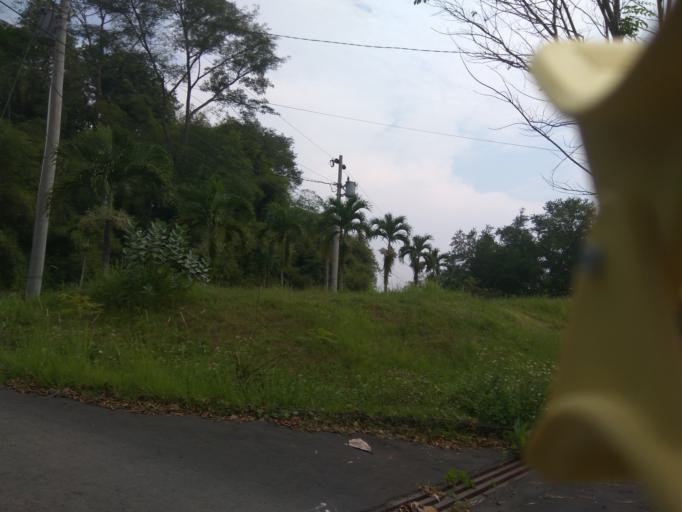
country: ID
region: Central Java
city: Semarang
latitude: -7.0426
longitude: 110.4161
